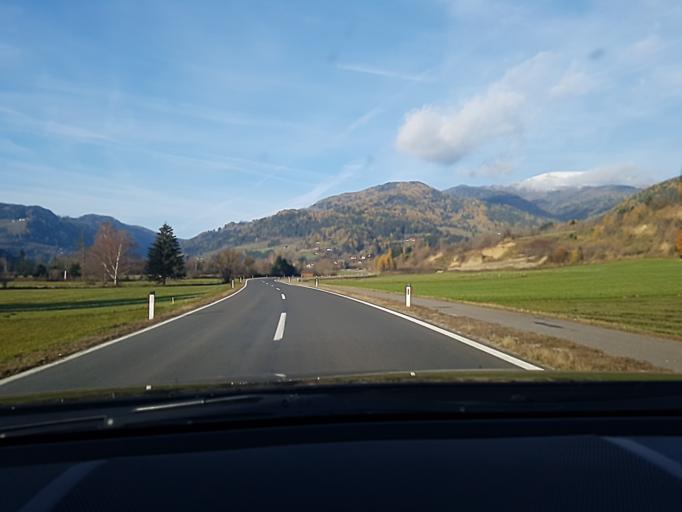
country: AT
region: Styria
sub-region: Politischer Bezirk Murau
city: Sankt Peter am Kammersberg
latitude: 47.1894
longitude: 14.1475
